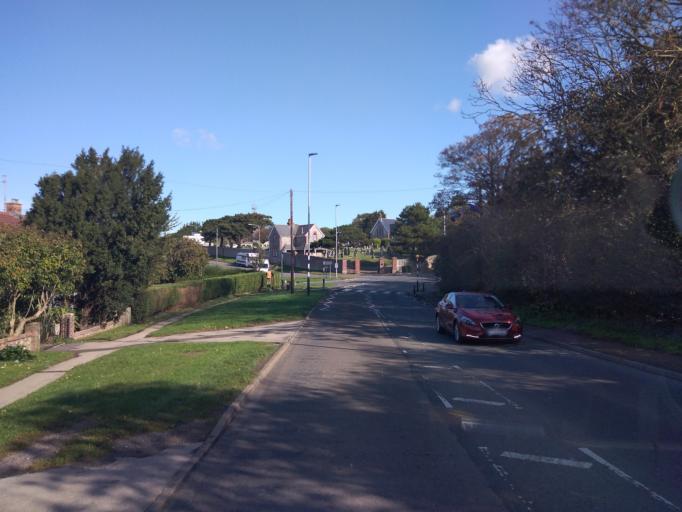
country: GB
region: England
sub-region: East Sussex
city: Seaford
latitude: 50.7804
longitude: 0.1204
